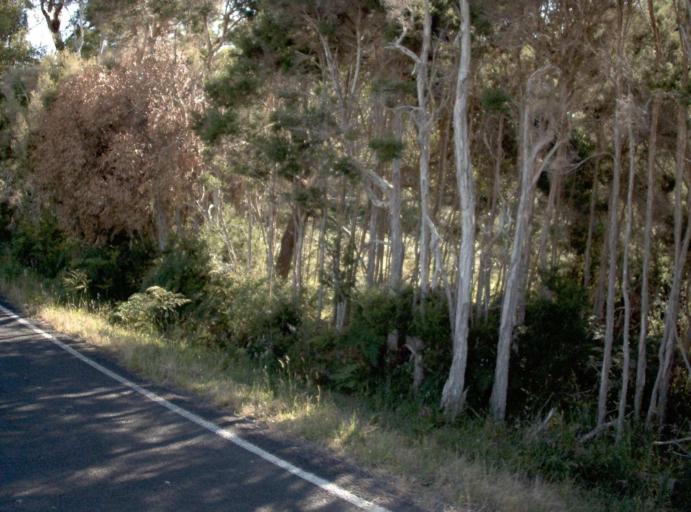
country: AU
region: Victoria
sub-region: Latrobe
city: Morwell
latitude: -38.7021
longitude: 146.3985
